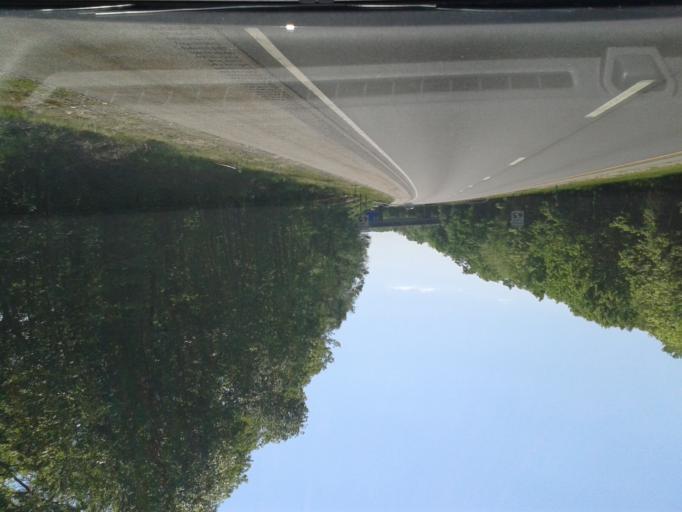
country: US
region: Rhode Island
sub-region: Washington County
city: Ashaway
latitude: 41.4330
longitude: -71.8116
